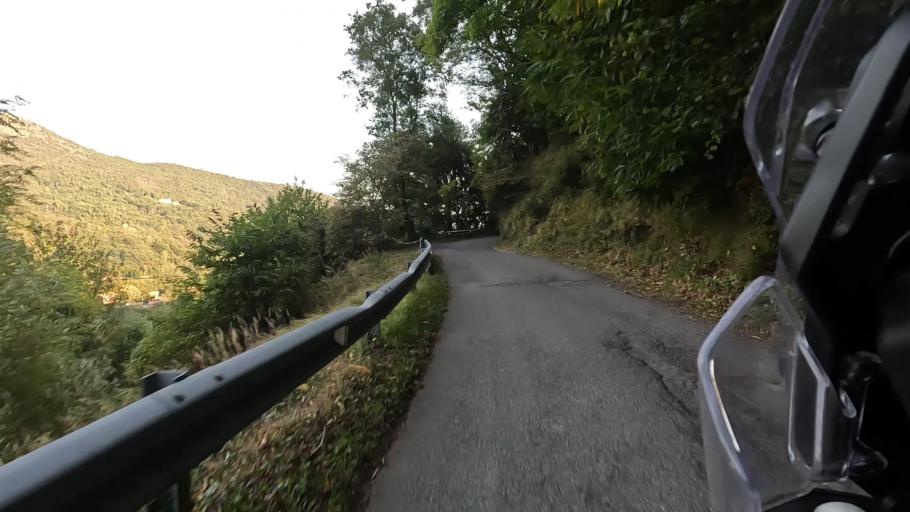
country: IT
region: Liguria
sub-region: Provincia di Savona
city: San Giovanni
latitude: 44.3991
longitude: 8.5336
